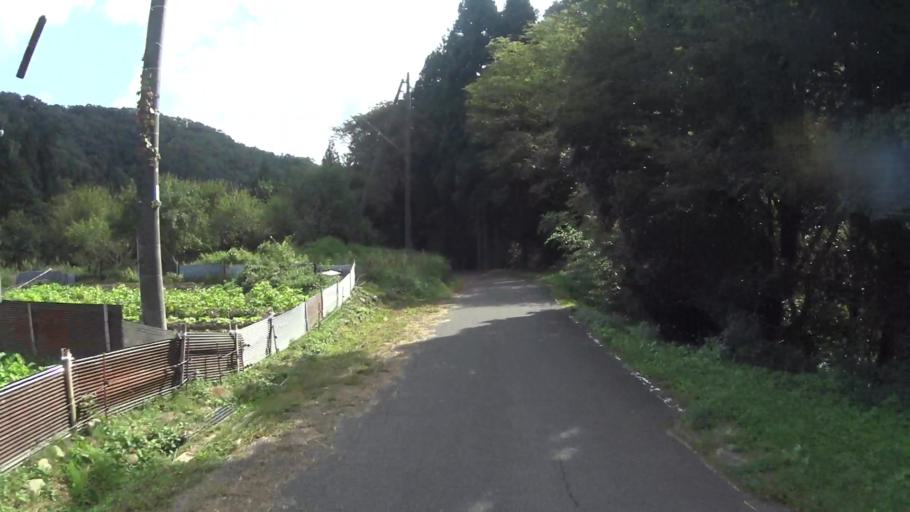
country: JP
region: Kyoto
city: Miyazu
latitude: 35.6114
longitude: 135.2007
